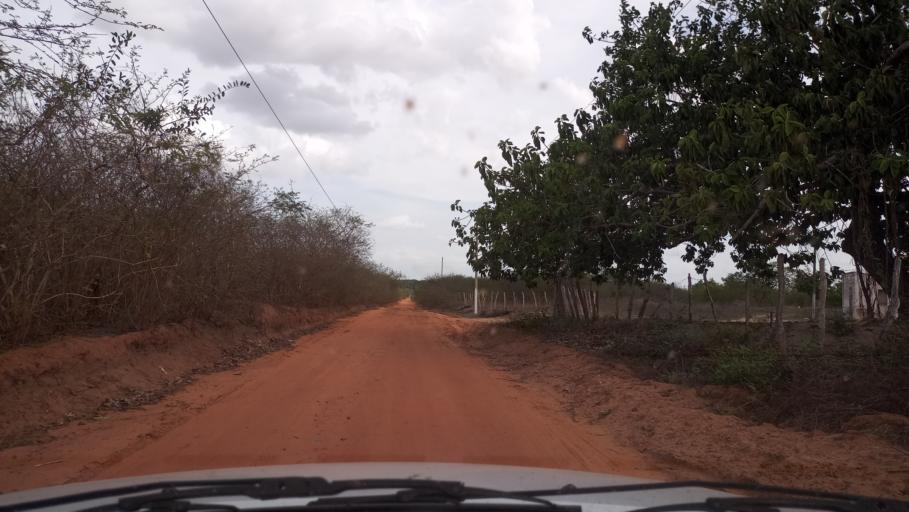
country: BR
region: Rio Grande do Norte
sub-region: Joao Camara
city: Joao Camara
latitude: -5.4984
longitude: -35.8263
